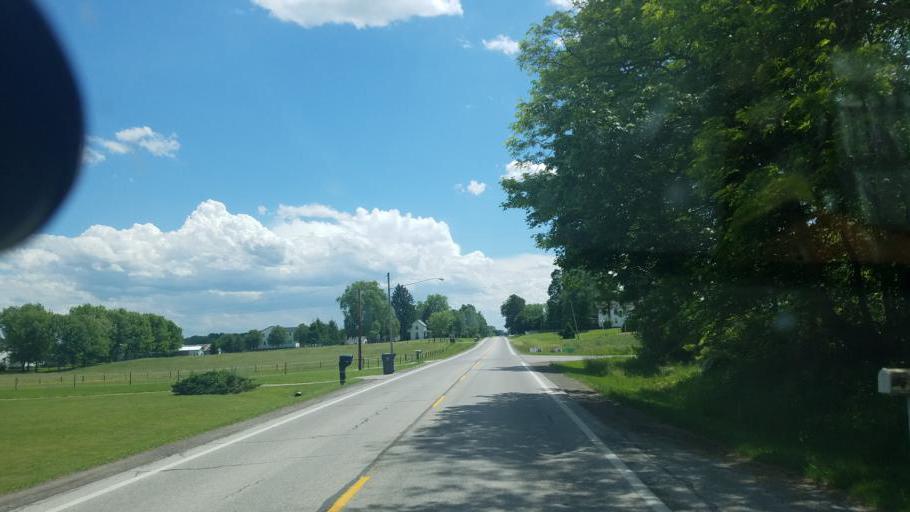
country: US
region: Ohio
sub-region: Geauga County
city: Middlefield
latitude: 41.4486
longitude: -80.9550
